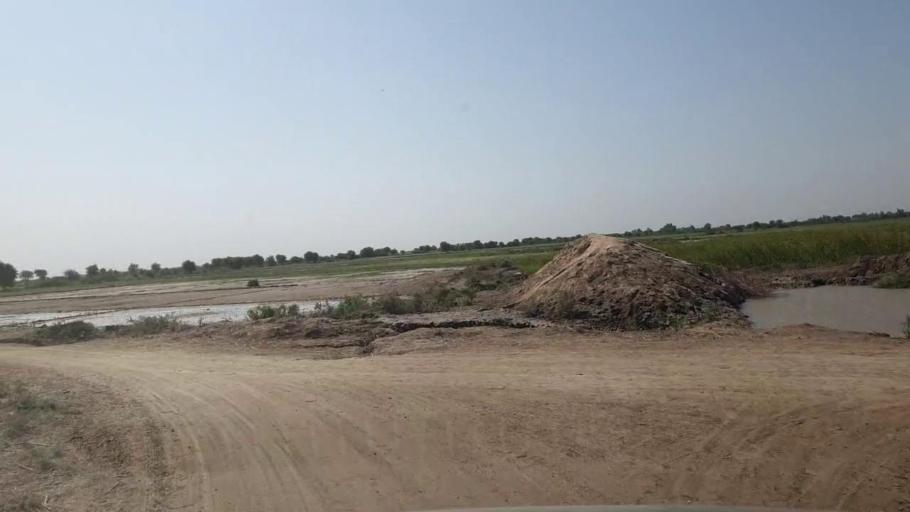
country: PK
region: Sindh
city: Tando Bago
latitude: 24.7383
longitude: 69.0214
